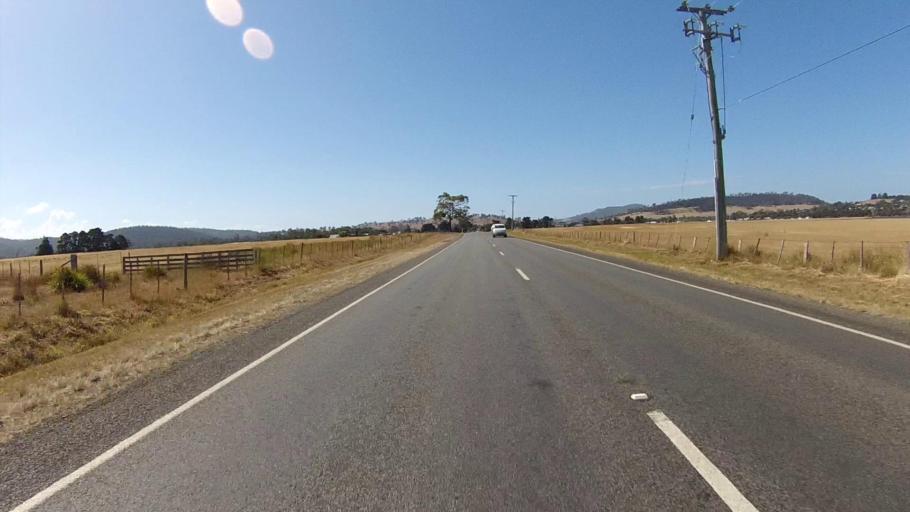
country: AU
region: Tasmania
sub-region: Sorell
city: Sorell
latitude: -42.5173
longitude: 147.9020
